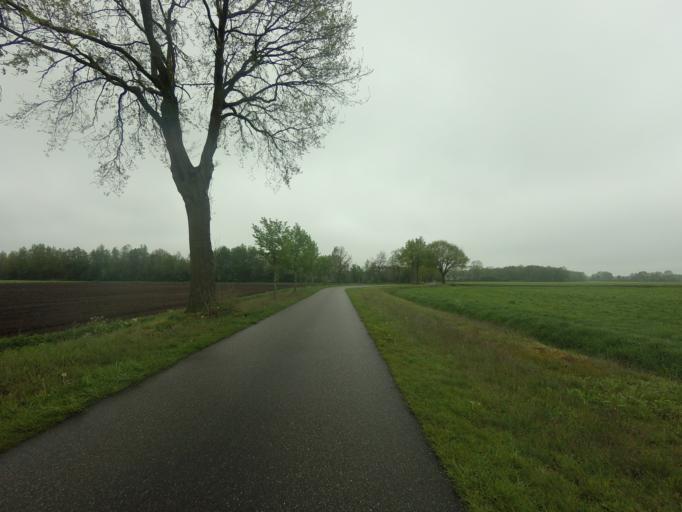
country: DE
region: North Rhine-Westphalia
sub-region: Regierungsbezirk Munster
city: Vreden
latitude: 52.1316
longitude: 6.8508
